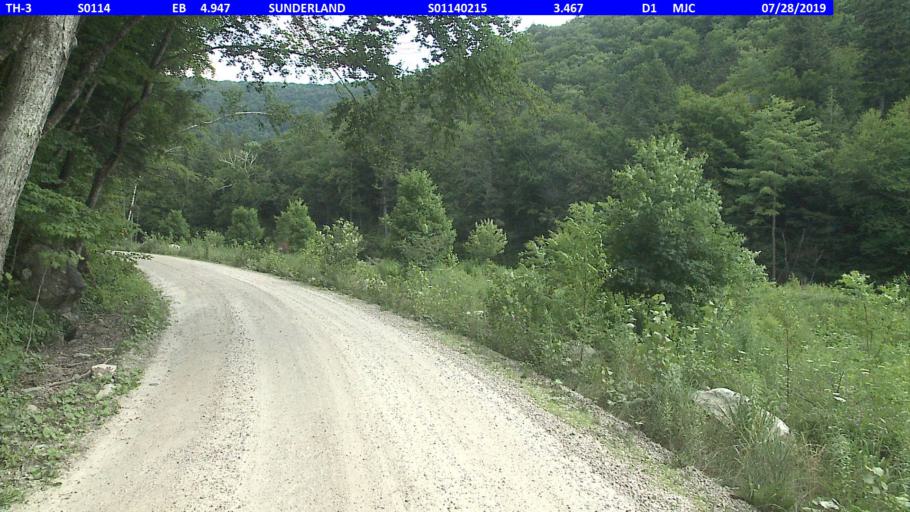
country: US
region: Vermont
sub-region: Bennington County
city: Arlington
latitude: 43.0427
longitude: -73.0940
